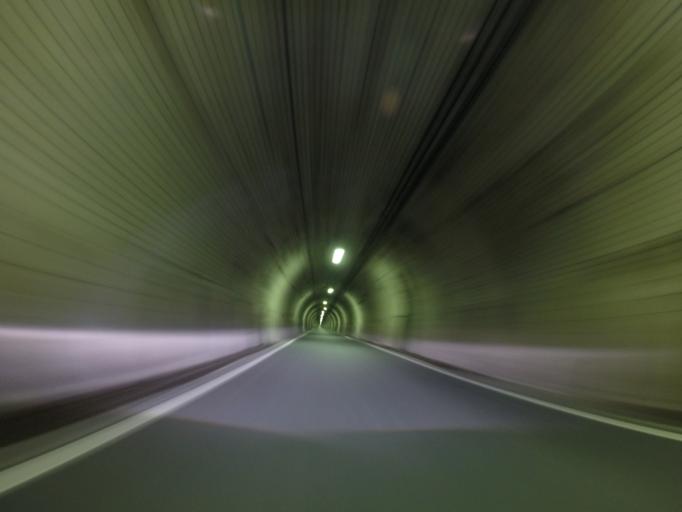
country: JP
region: Shizuoka
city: Mori
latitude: 34.8425
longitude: 138.0089
